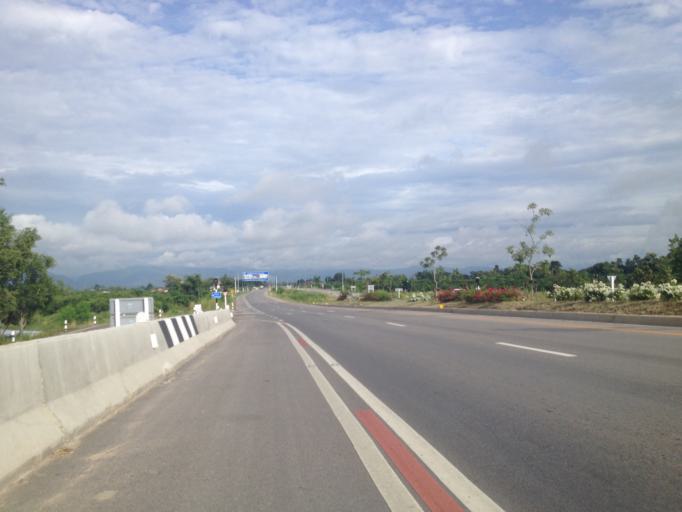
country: TH
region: Lamphun
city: Pa Sang
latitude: 18.5382
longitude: 98.8564
